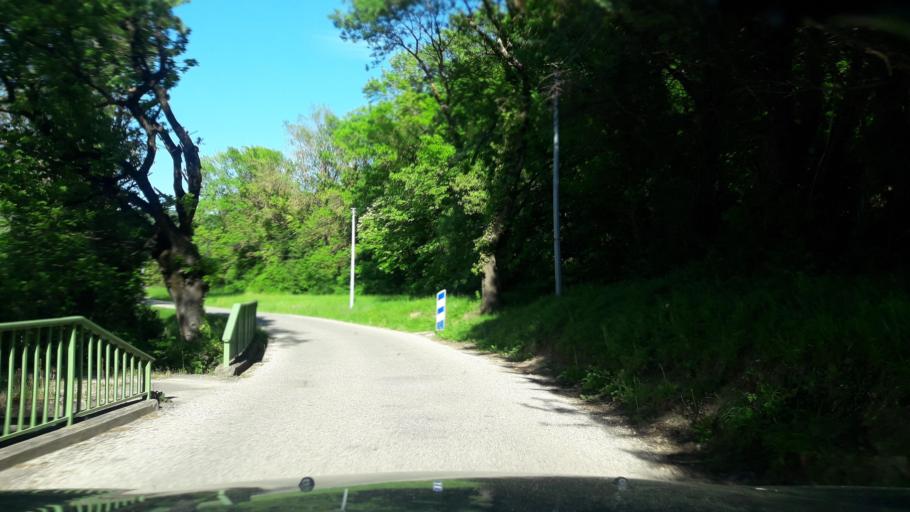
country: FR
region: Rhone-Alpes
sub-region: Departement de la Drome
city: Saulce-sur-Rhone
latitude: 44.7024
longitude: 4.8534
